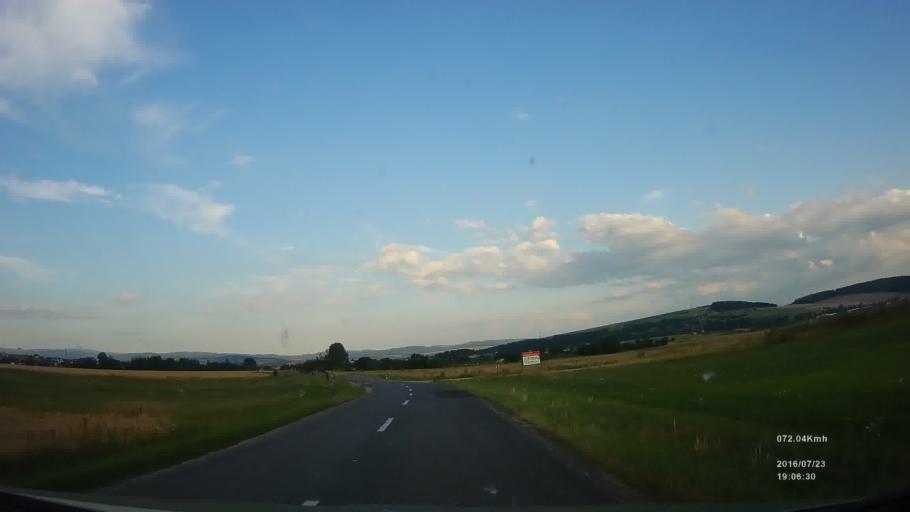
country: SK
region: Presovsky
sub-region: Okres Poprad
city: Nova Lesna
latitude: 49.1230
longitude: 20.3404
